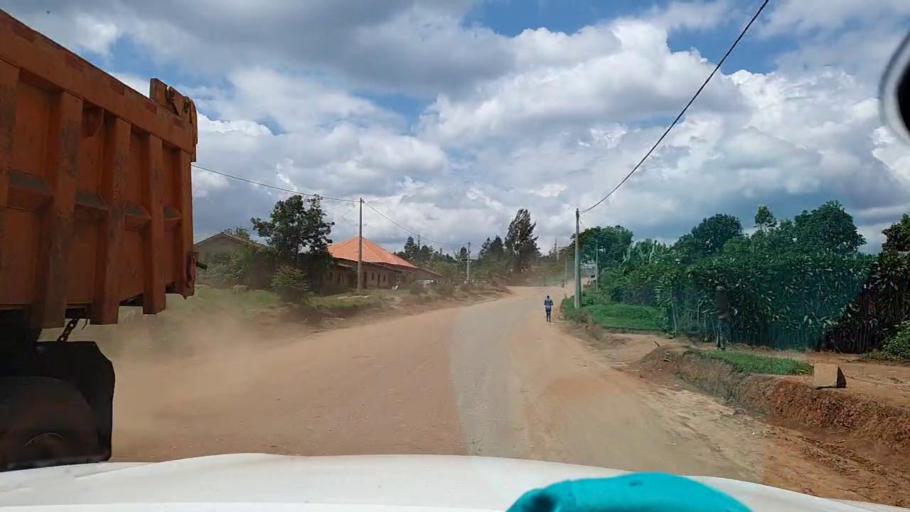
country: RW
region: Southern Province
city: Nzega
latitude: -2.6497
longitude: 29.5593
